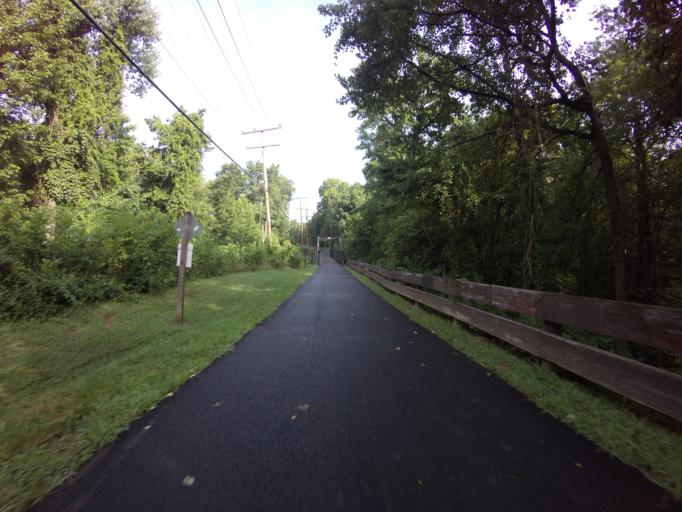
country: US
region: Maryland
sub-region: Anne Arundel County
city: South Gate
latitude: 39.1421
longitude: -76.6078
